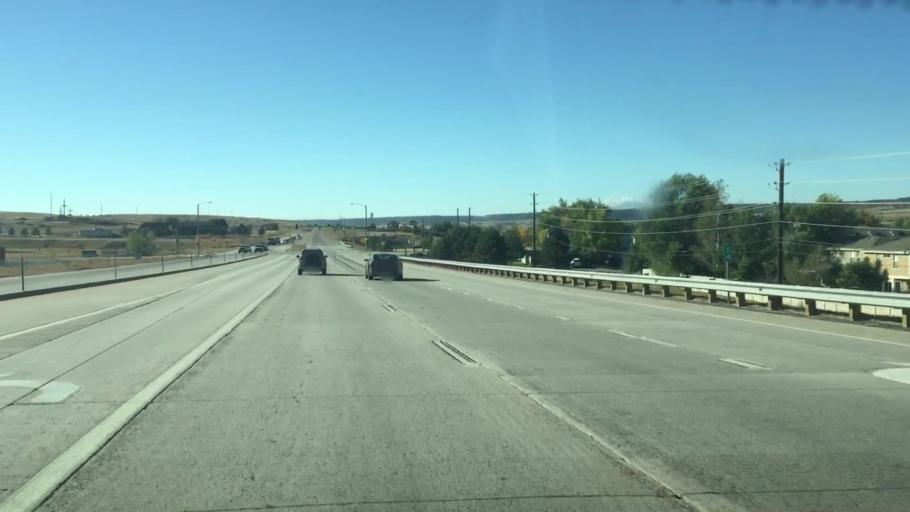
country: US
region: Colorado
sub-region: Douglas County
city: The Pinery
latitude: 39.4371
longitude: -104.7603
